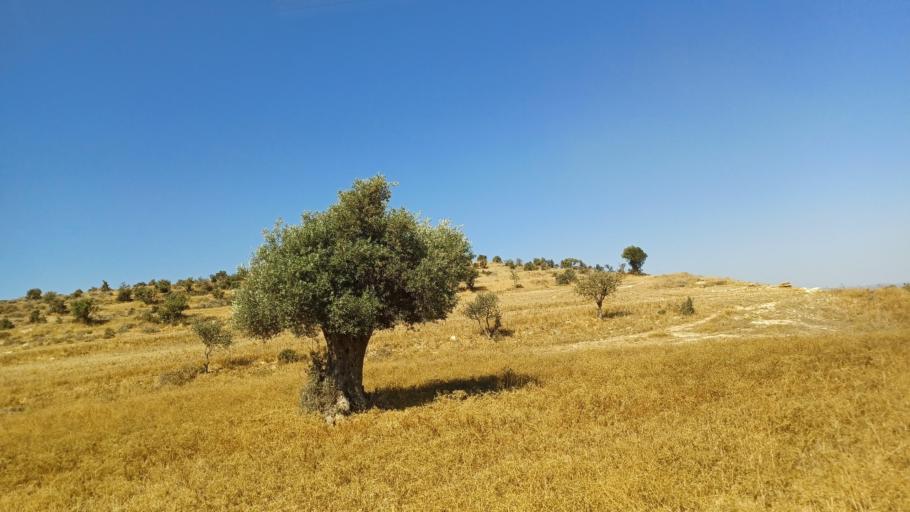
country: CY
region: Larnaka
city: Psevdas
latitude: 34.9657
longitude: 33.4775
